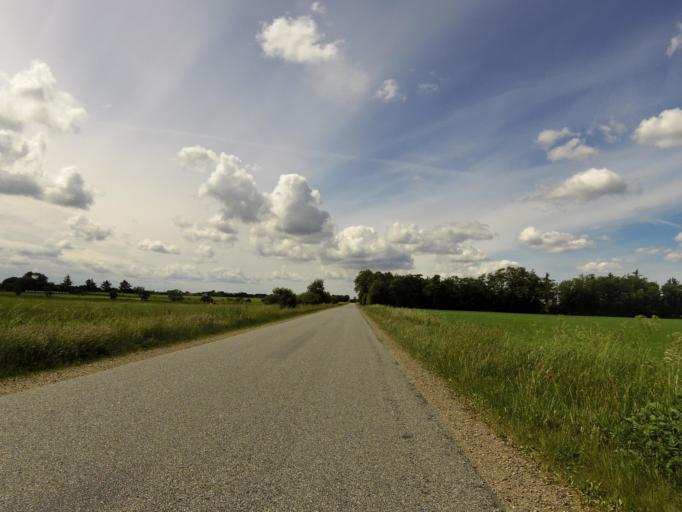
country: DK
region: South Denmark
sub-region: Esbjerg Kommune
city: Ribe
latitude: 55.2605
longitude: 8.8343
